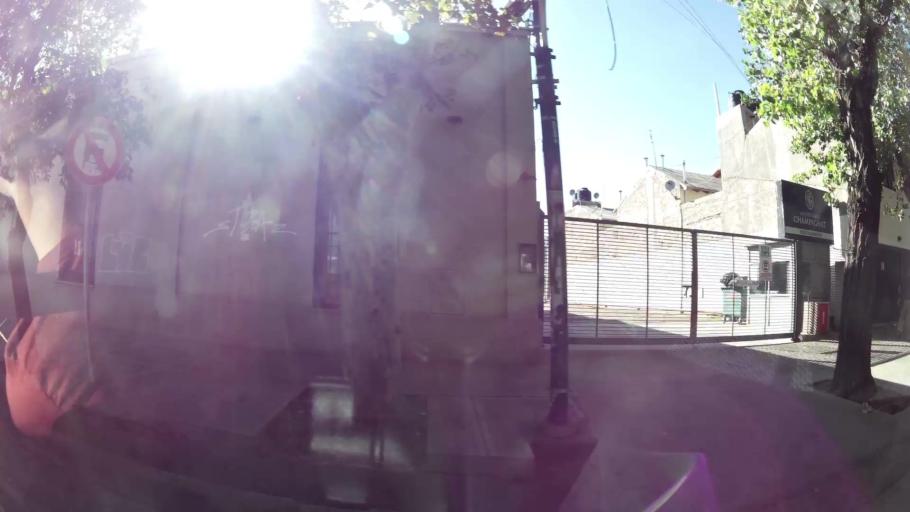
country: AR
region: Mendoza
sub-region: Departamento de Godoy Cruz
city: Godoy Cruz
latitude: -32.9171
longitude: -68.8429
